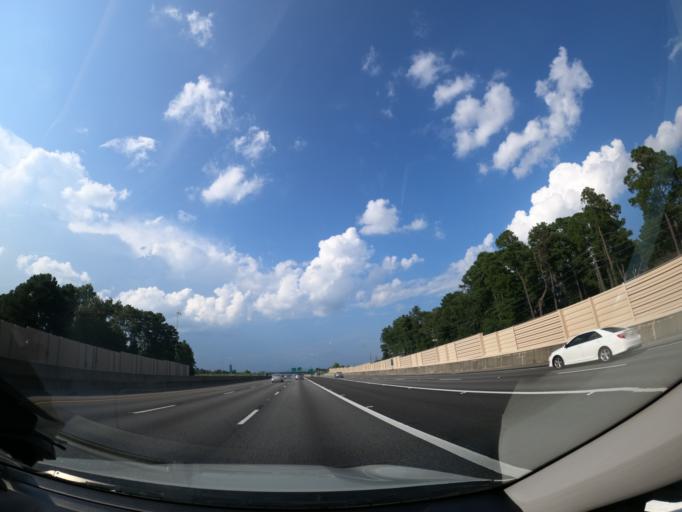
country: US
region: Georgia
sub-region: Columbia County
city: Martinez
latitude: 33.4789
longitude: -82.0853
